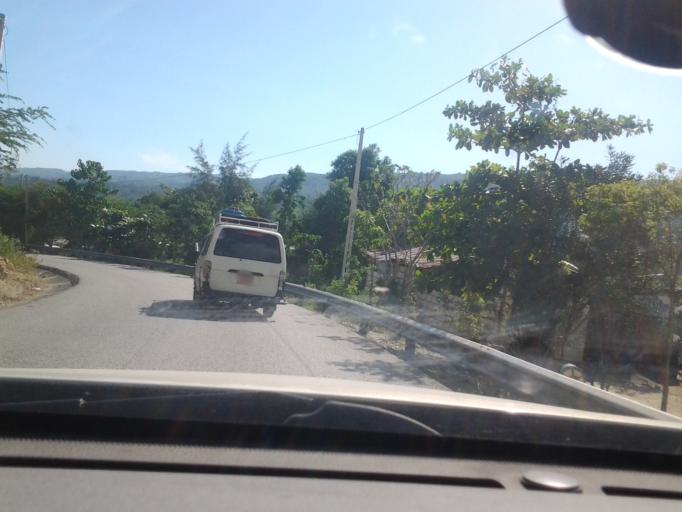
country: HT
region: Sud-Est
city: Jacmel
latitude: 18.2798
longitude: -72.5703
